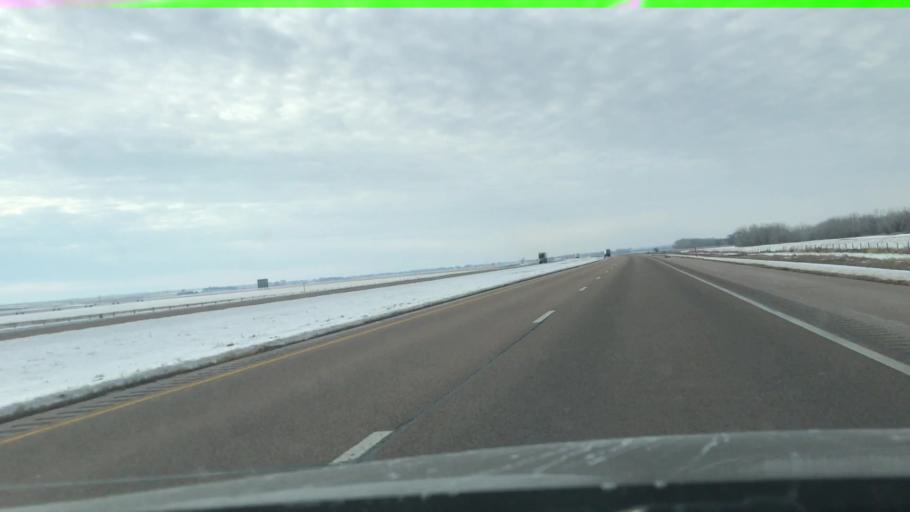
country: US
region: Nebraska
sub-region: Keith County
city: Ogallala
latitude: 41.1202
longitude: -101.6157
